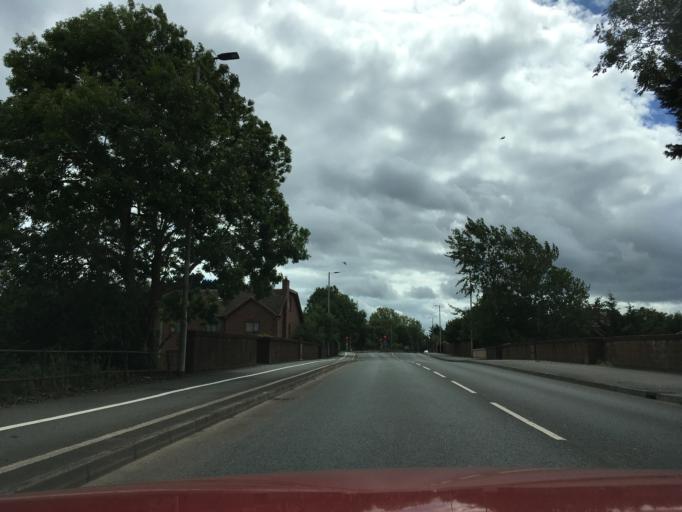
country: GB
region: England
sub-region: Devon
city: Heavitree
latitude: 50.7232
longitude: -3.4800
